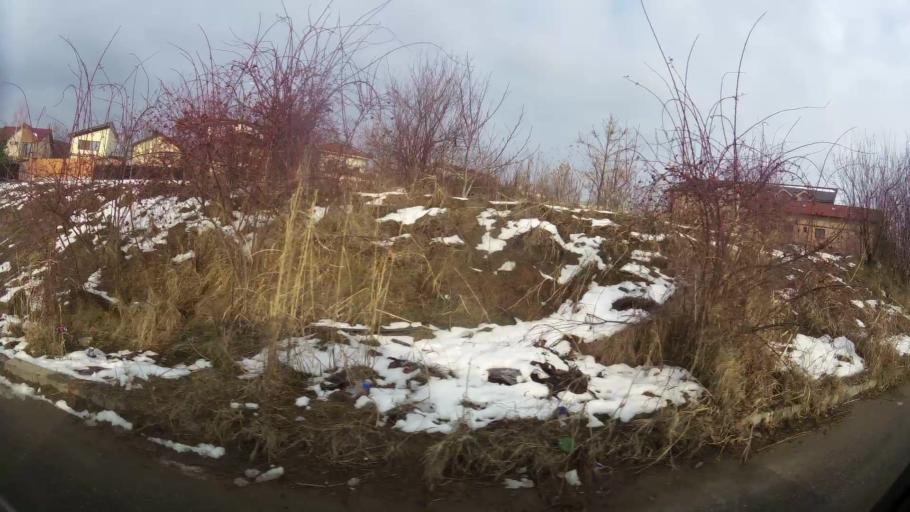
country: RO
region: Ilfov
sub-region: Comuna Popesti-Leordeni
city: Popesti-Leordeni
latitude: 44.4018
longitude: 26.1733
